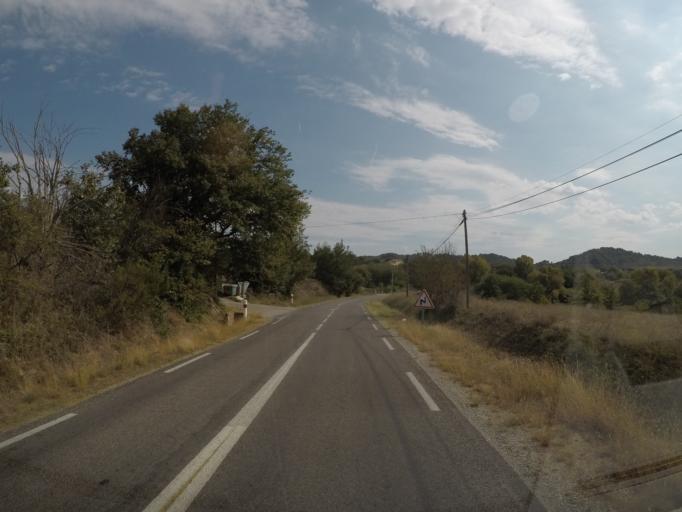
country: FR
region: Provence-Alpes-Cote d'Azur
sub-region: Departement du Vaucluse
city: Ansouis
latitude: 43.7359
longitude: 5.4814
